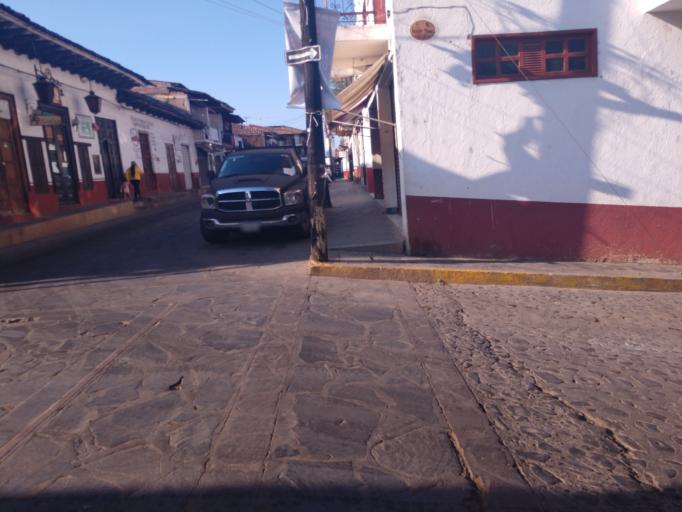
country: MX
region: Jalisco
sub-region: Mazamitla
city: Mazamitla
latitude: 19.9169
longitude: -103.0195
